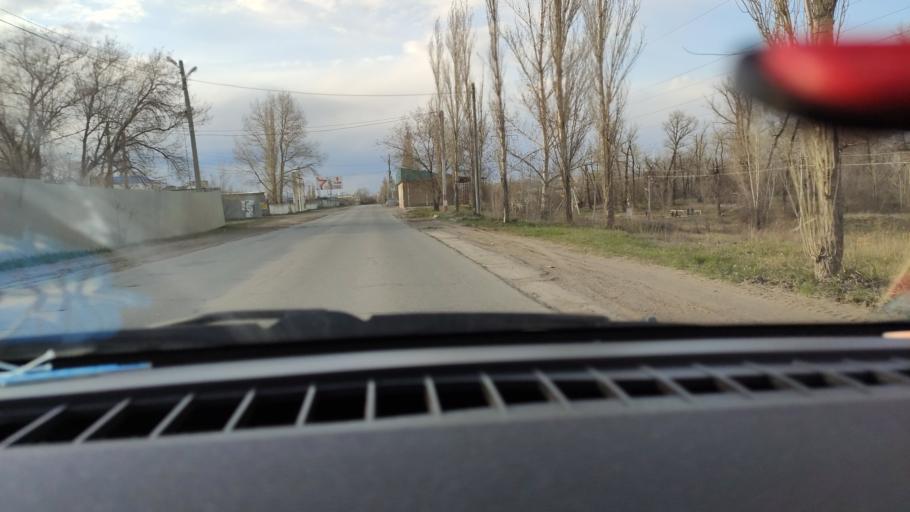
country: RU
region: Saratov
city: Engel's
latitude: 51.4885
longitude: 46.0519
